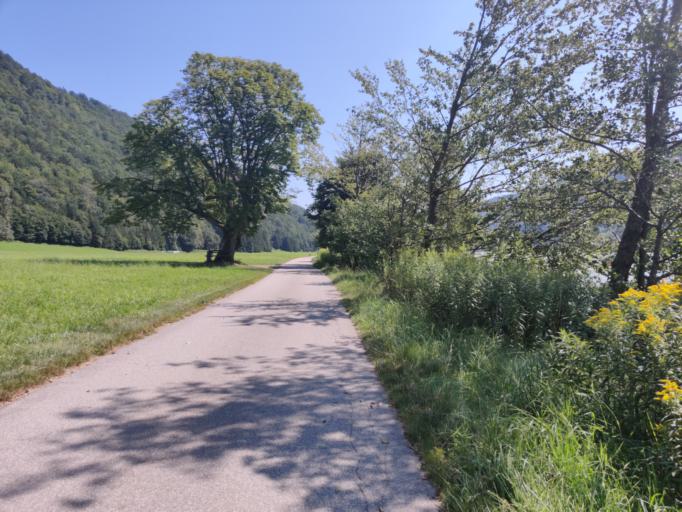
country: AT
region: Upper Austria
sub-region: Politischer Bezirk Rohrbach
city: Pfarrkirchen im Muehlkreis
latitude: 48.4471
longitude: 13.8307
